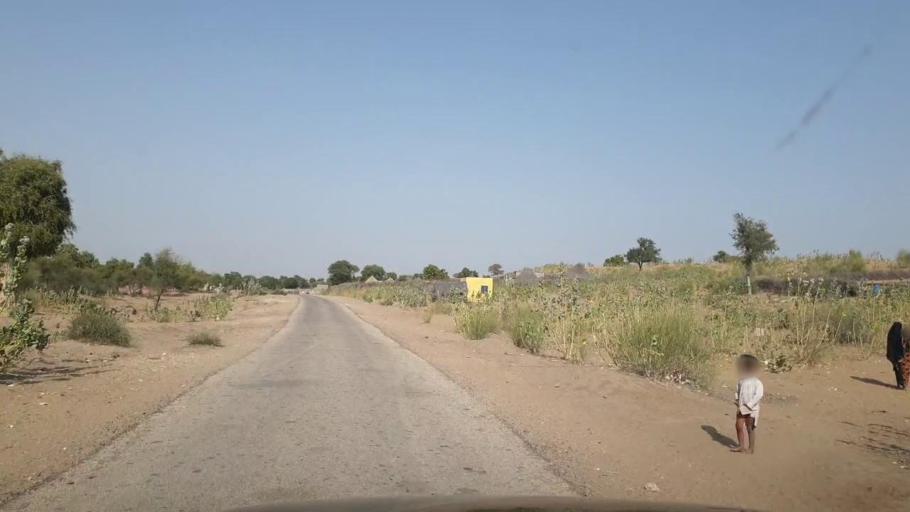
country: PK
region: Sindh
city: Islamkot
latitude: 25.1301
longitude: 70.4549
